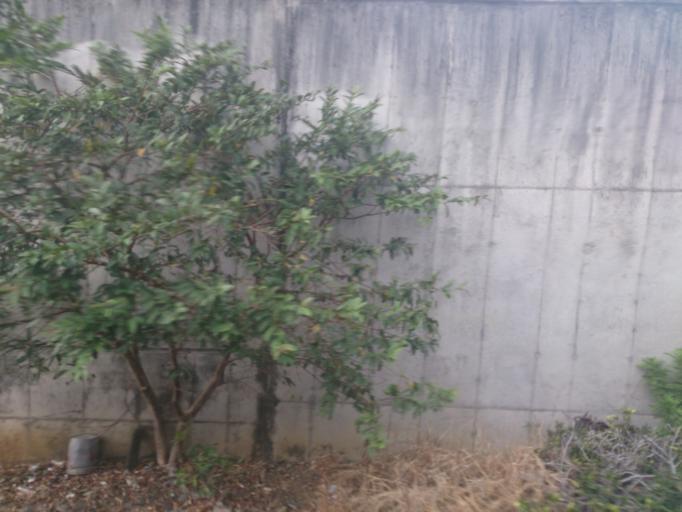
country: CR
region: San Jose
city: San Rafael
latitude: 9.9372
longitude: -84.1172
